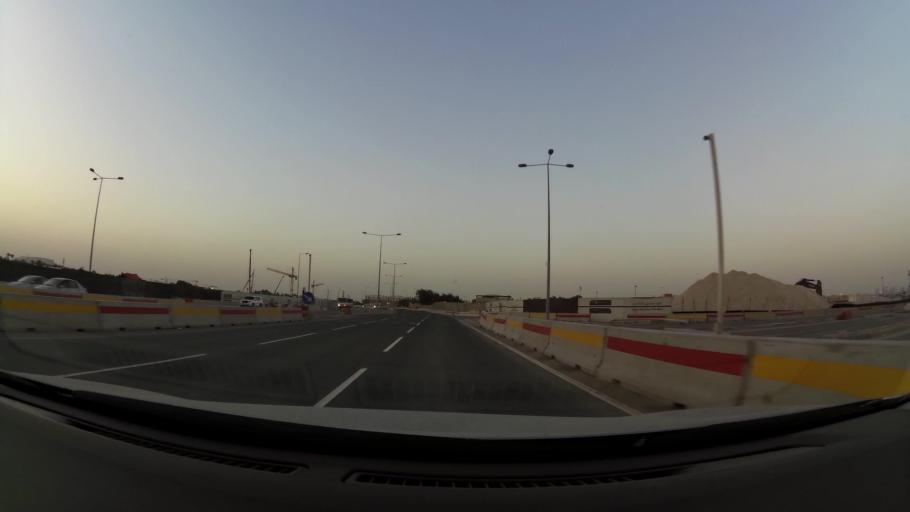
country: QA
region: Baladiyat ar Rayyan
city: Ar Rayyan
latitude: 25.2942
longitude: 51.4661
